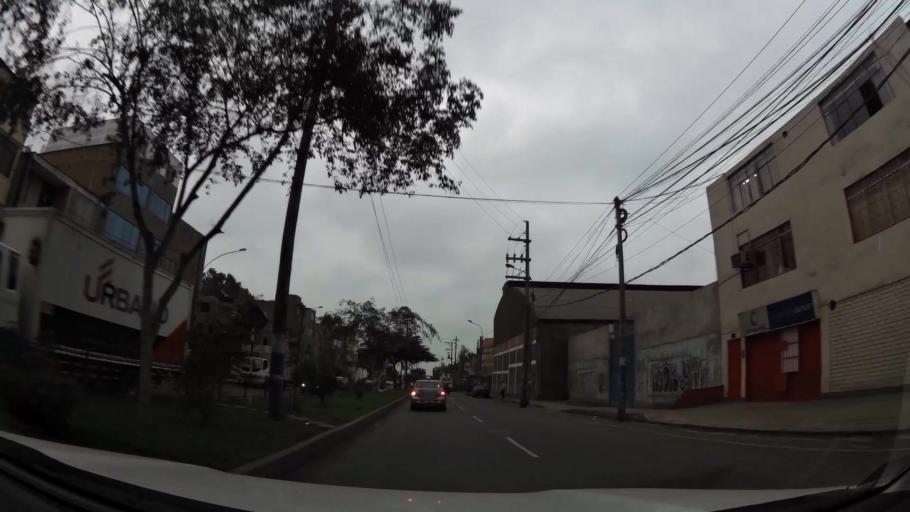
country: PE
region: Lima
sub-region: Lima
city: San Luis
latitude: -12.0701
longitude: -76.9809
